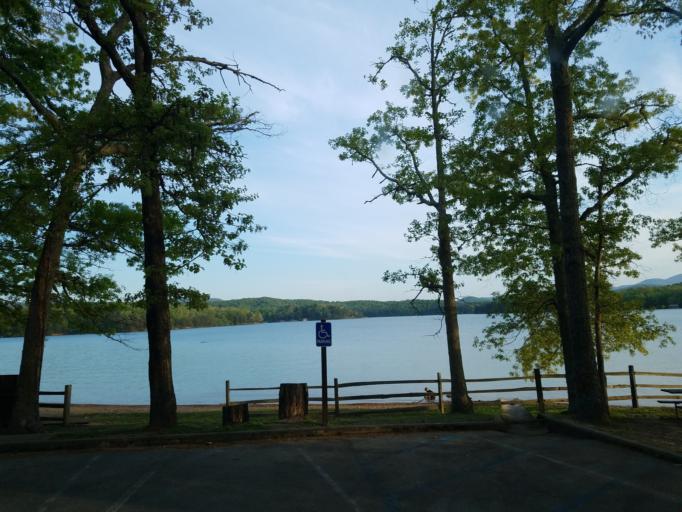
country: US
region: Georgia
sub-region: Fannin County
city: Blue Ridge
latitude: 34.8686
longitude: -84.2536
